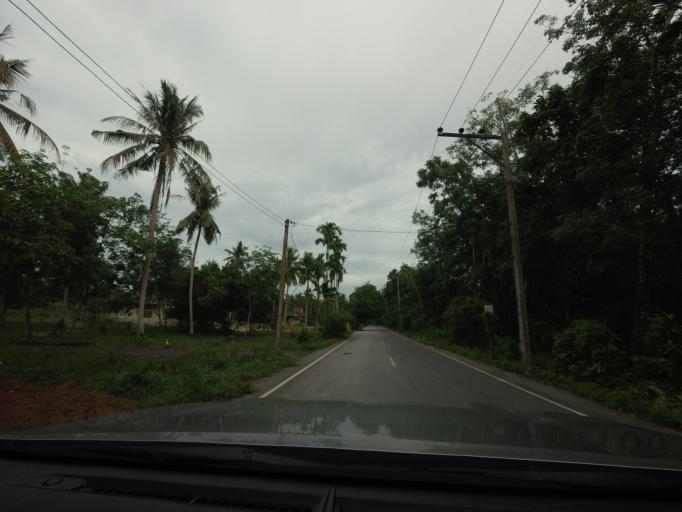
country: TH
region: Nakhon Si Thammarat
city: Phra Phrom
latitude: 8.2793
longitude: 99.9428
